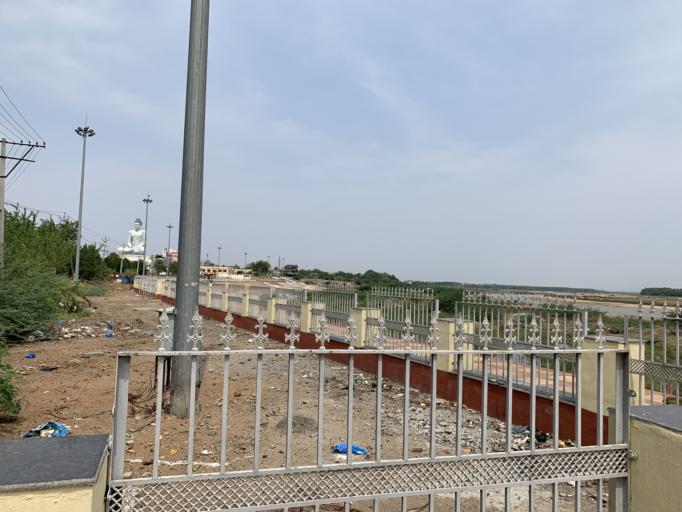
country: IN
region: Andhra Pradesh
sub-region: Krishna
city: Kondapalle
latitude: 16.5808
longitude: 80.3564
